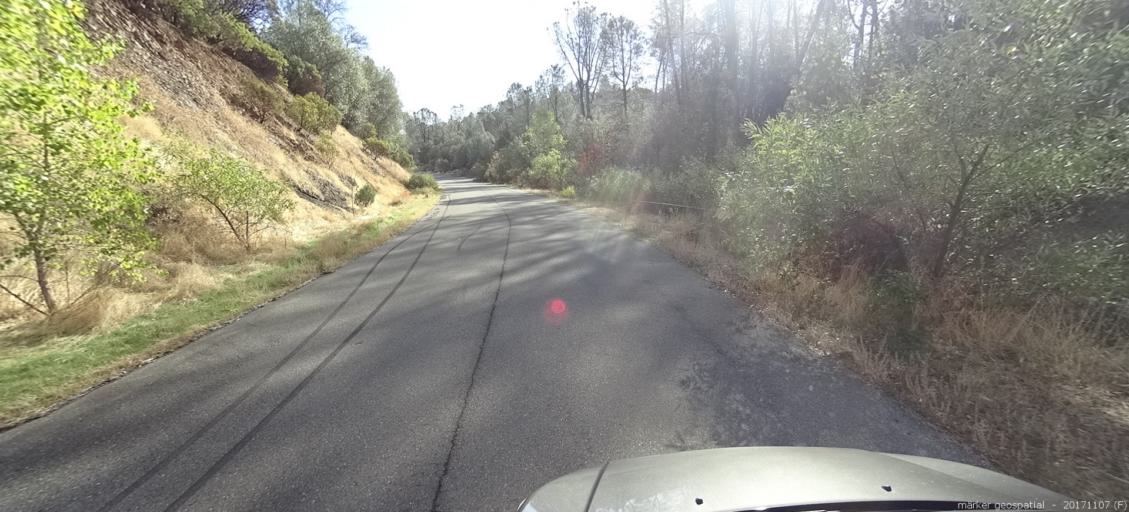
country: US
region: California
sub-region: Shasta County
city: Redding
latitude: 40.5687
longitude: -122.4431
